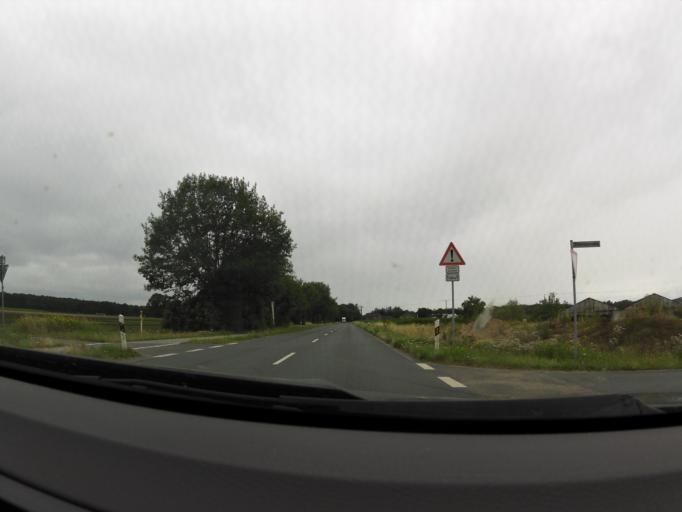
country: DE
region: North Rhine-Westphalia
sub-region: Regierungsbezirk Dusseldorf
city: Kevelaer
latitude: 51.5487
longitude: 6.2337
